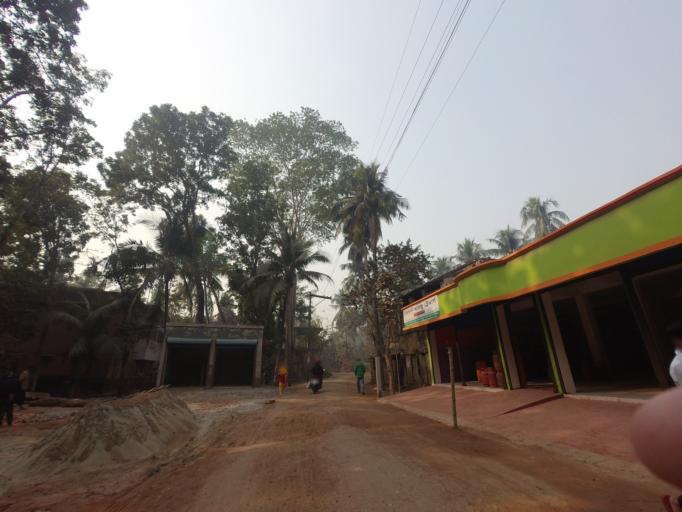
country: BD
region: Khulna
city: Narail
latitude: 23.1115
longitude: 89.4972
